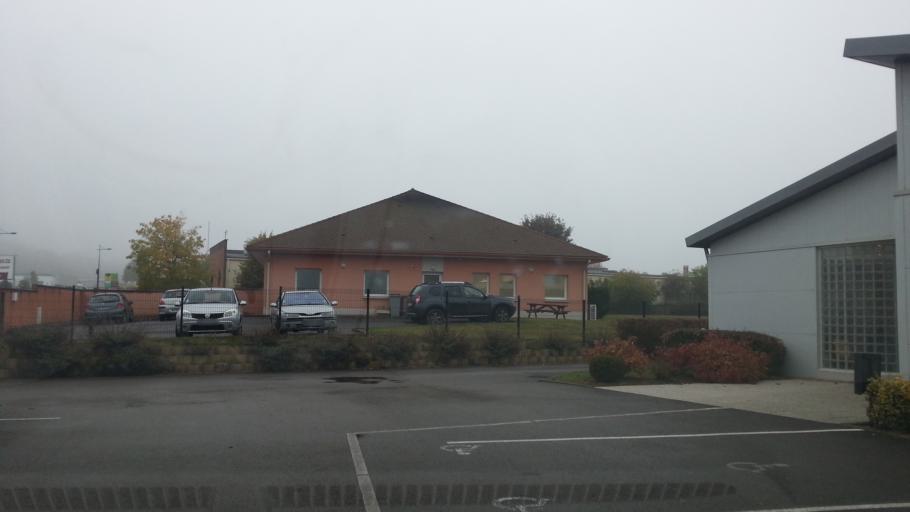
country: FR
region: Picardie
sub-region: Departement de l'Oise
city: Fitz-James
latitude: 49.3942
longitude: 2.4194
